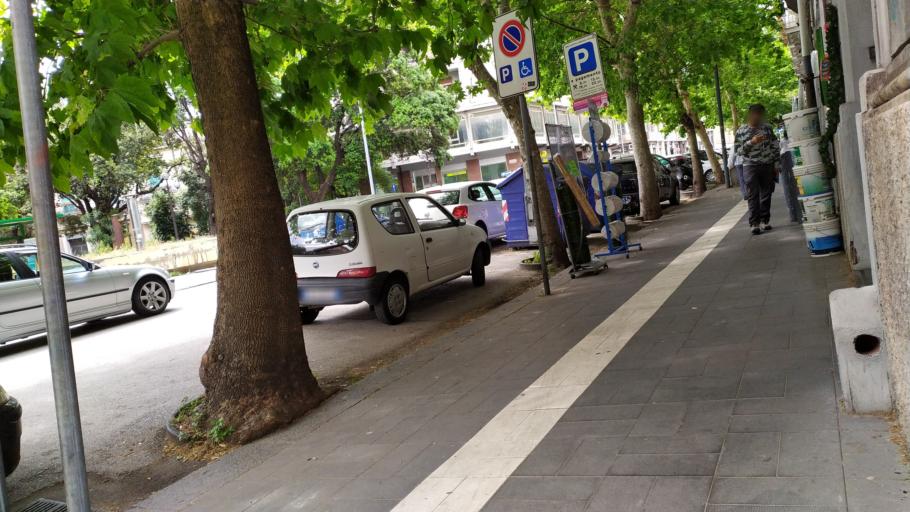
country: IT
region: Sicily
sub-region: Messina
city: Messina
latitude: 38.1960
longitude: 15.5555
